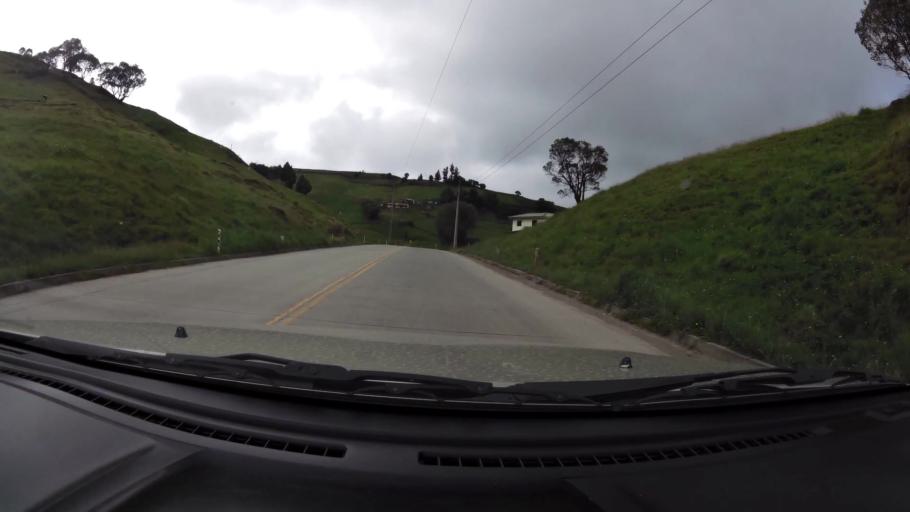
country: EC
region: Canar
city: Canar
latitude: -2.6195
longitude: -78.9164
